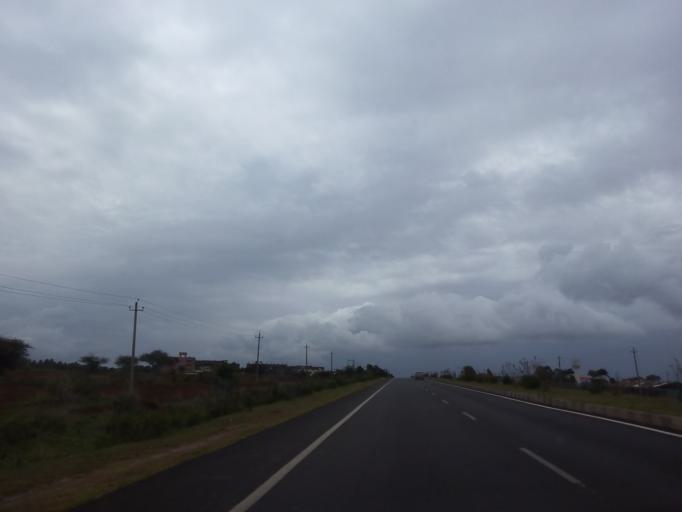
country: IN
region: Karnataka
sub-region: Haveri
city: Ranibennur
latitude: 14.5757
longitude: 75.6874
